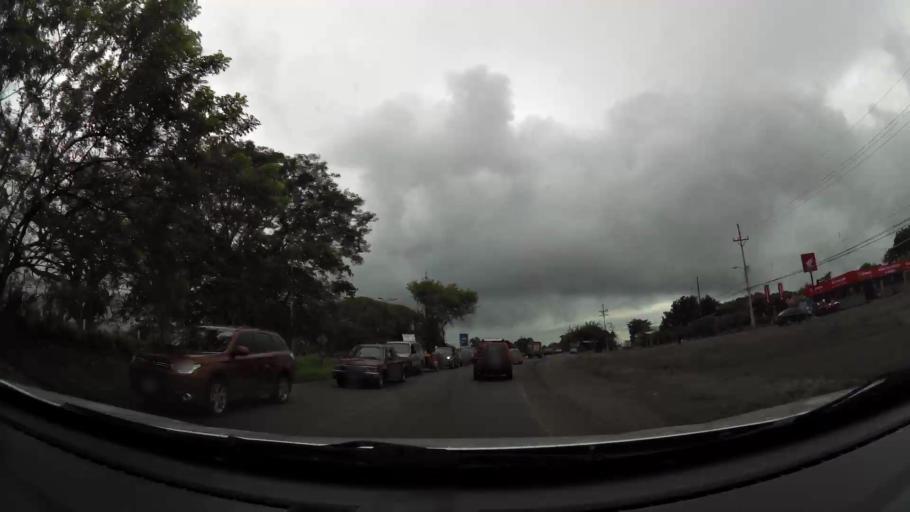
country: CR
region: Puntarenas
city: Esparza
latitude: 9.9973
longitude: -84.6740
